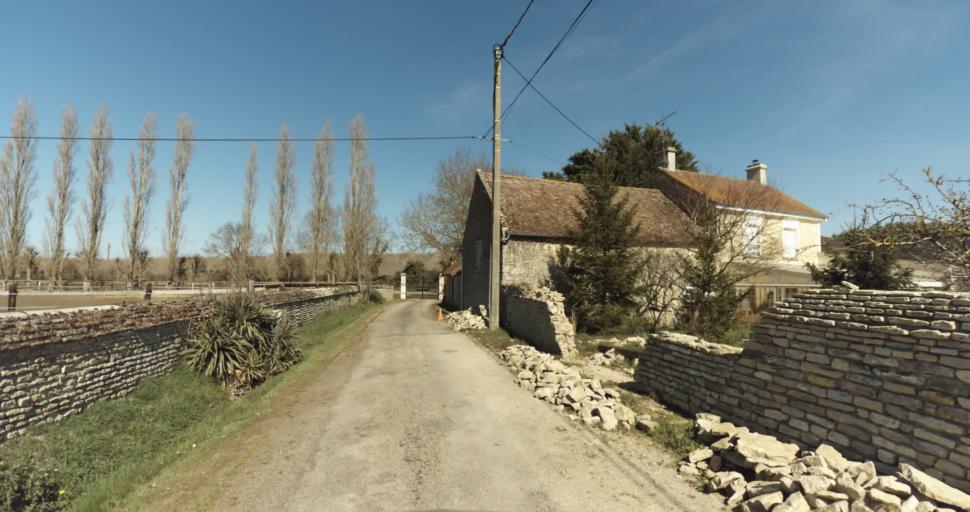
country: FR
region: Lower Normandy
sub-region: Departement du Calvados
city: Saint-Pierre-sur-Dives
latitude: 49.0525
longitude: -0.0502
